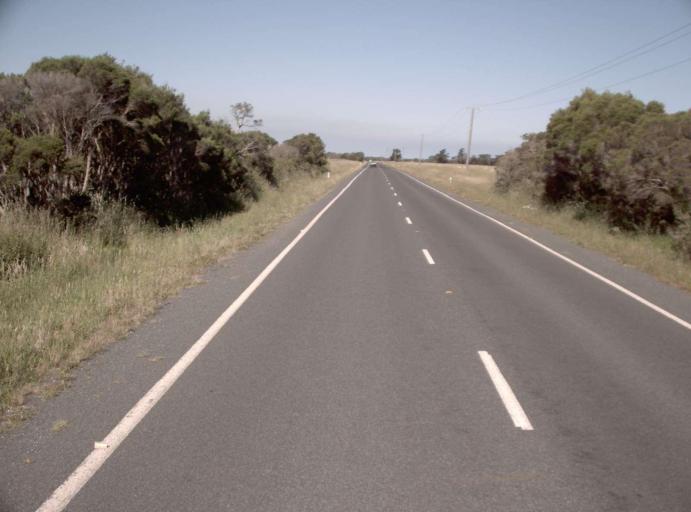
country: AU
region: Victoria
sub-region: Latrobe
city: Traralgon
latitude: -38.6264
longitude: 146.6265
